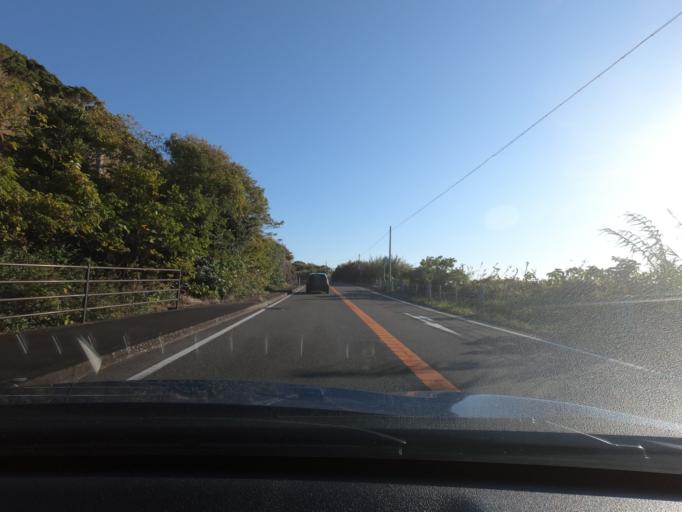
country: JP
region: Kagoshima
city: Akune
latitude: 31.9389
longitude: 130.2173
